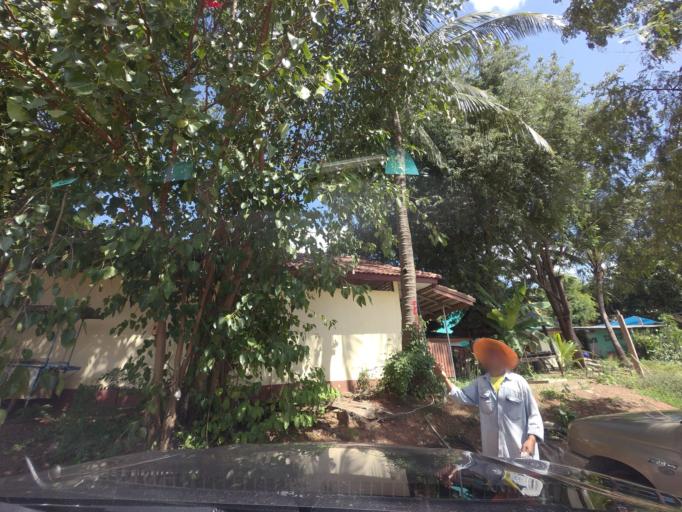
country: TH
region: Changwat Udon Thani
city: Ban Dung
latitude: 17.7442
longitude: 103.3579
